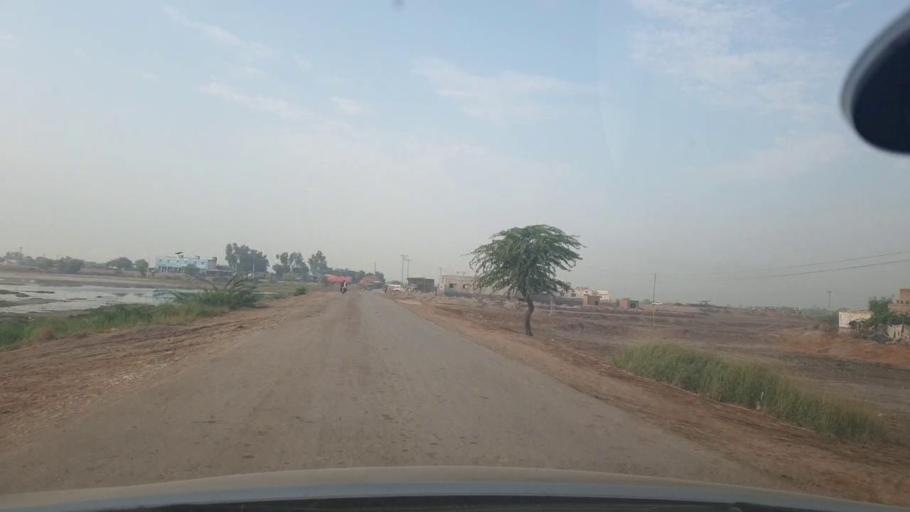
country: PK
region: Sindh
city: Jacobabad
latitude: 28.2655
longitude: 68.4184
